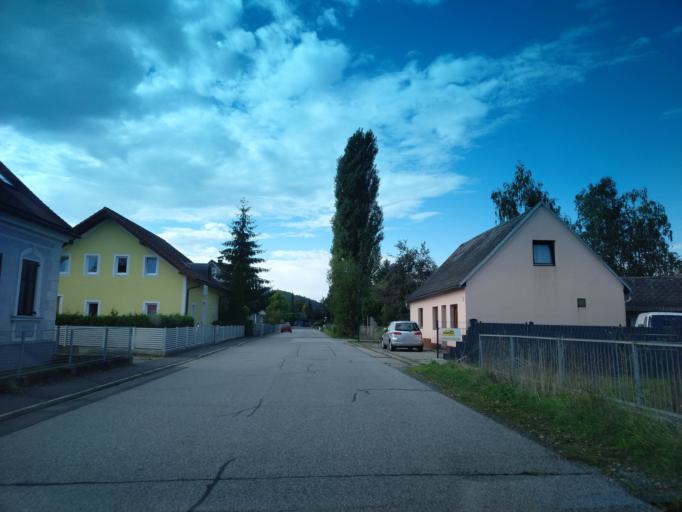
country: AT
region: Styria
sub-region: Politischer Bezirk Leibnitz
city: Kaindorf an der Sulm
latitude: 46.7888
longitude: 15.5370
